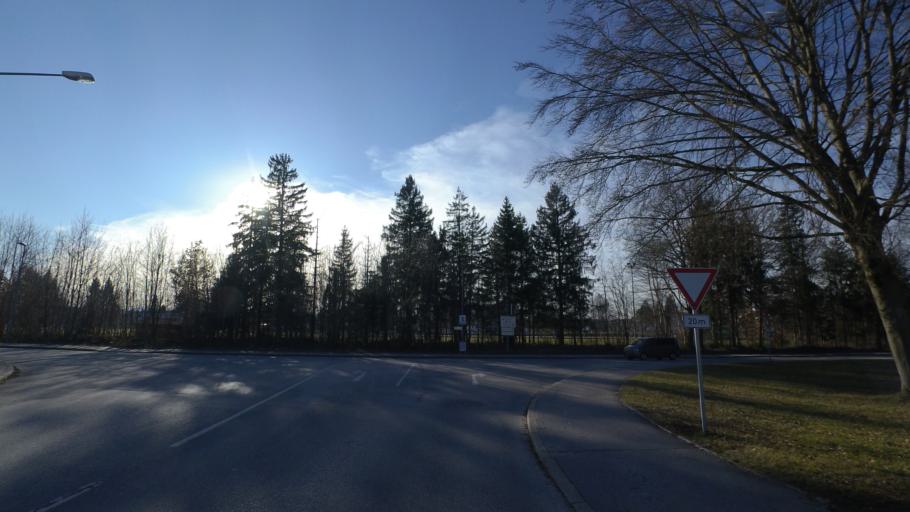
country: DE
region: Bavaria
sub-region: Upper Bavaria
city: Traunreut
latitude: 47.9609
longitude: 12.6056
